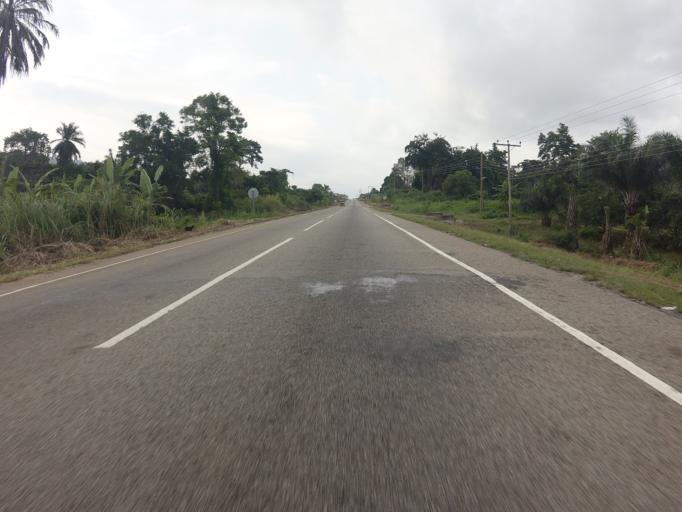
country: GH
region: Volta
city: Ho
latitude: 6.6552
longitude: 0.4704
